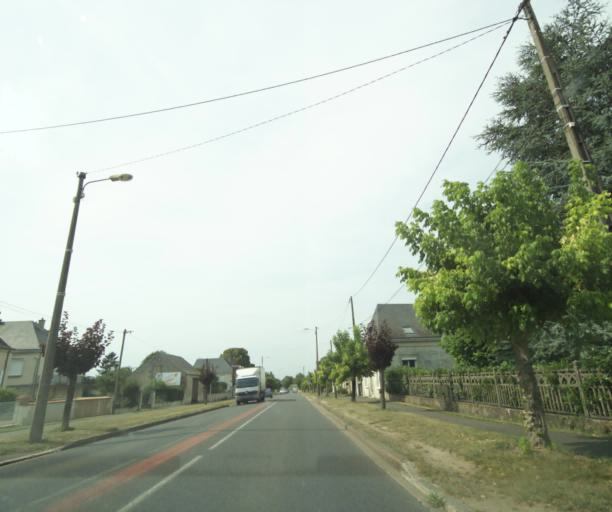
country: FR
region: Centre
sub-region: Departement d'Indre-et-Loire
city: Neuille-Pont-Pierre
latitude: 47.5488
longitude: 0.5508
